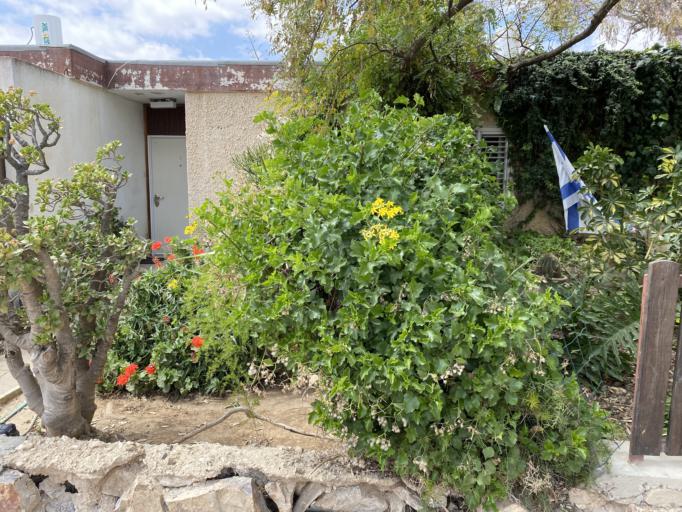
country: IL
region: Southern District
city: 'Arad
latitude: 31.2537
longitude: 35.2148
